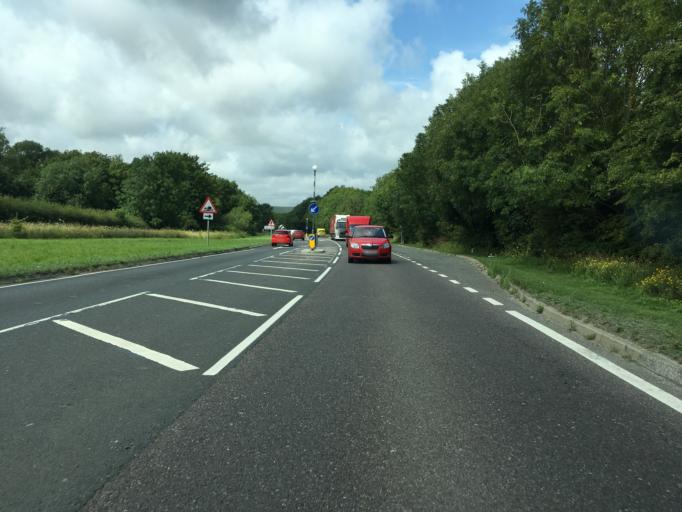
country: GB
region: England
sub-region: East Sussex
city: Ringmer
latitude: 50.8521
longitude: 0.1089
